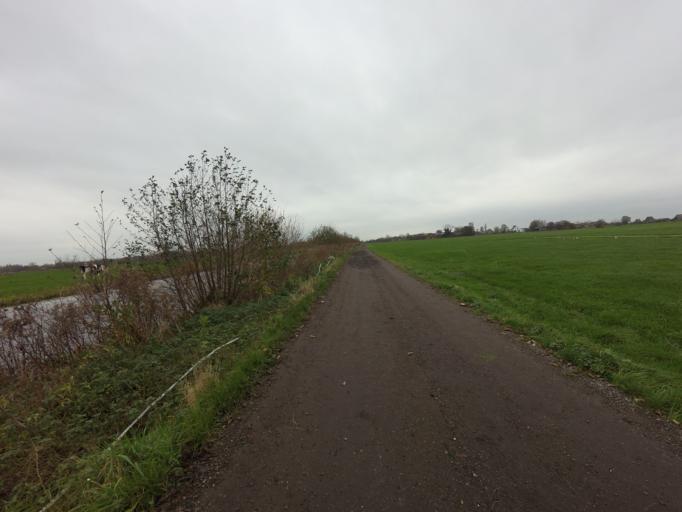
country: NL
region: Utrecht
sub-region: Gemeente Woerden
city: Woerden
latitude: 52.1298
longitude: 4.8998
